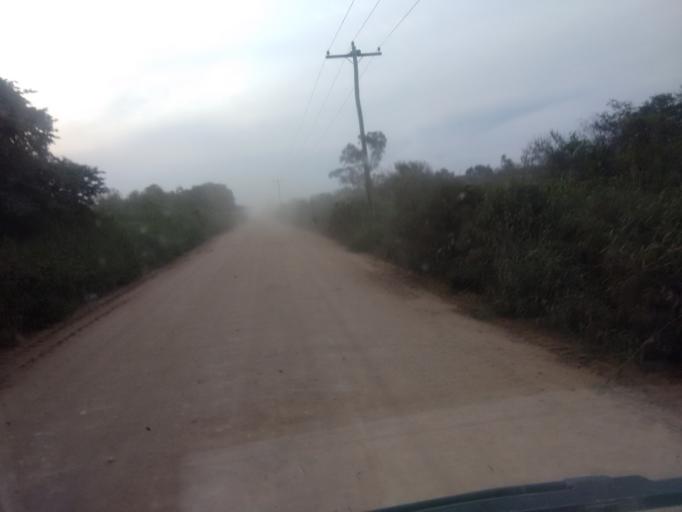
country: BR
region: Rio Grande do Sul
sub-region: Camaqua
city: Camaqua
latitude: -30.9300
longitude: -51.7907
